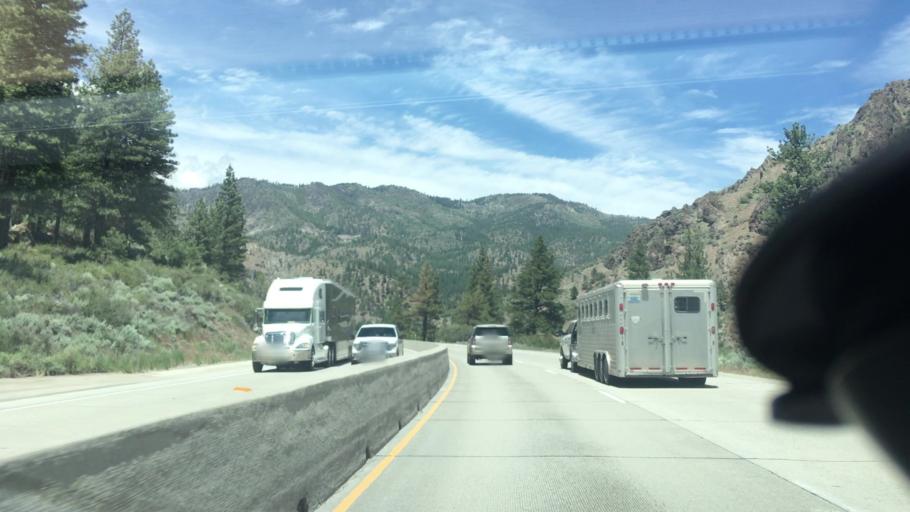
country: US
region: Nevada
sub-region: Washoe County
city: Verdi
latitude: 39.4146
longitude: -120.0287
